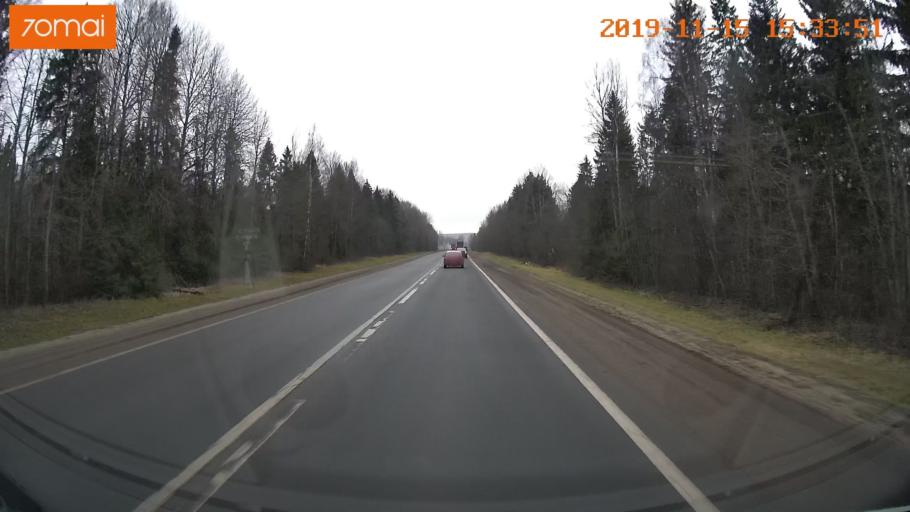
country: RU
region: Jaroslavl
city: Danilov
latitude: 58.0759
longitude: 40.0911
